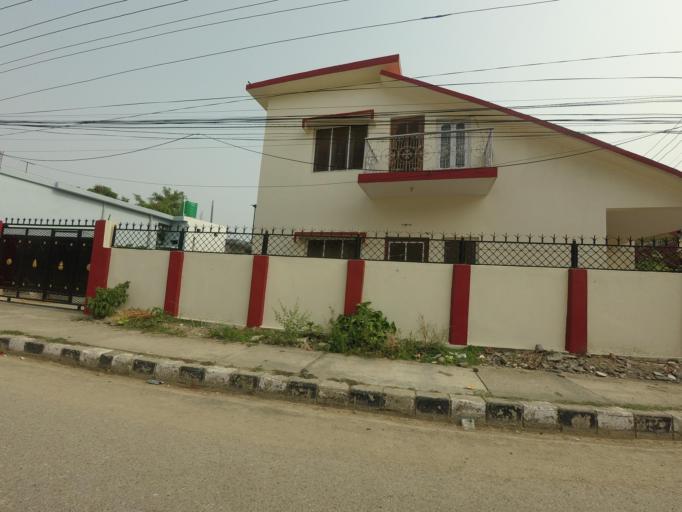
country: NP
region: Western Region
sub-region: Lumbini Zone
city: Bhairahawa
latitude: 27.5184
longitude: 83.4586
